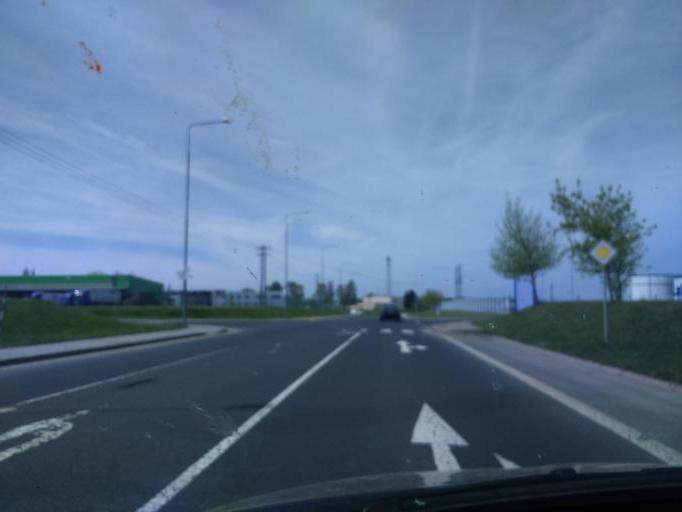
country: CZ
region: Karlovarsky
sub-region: Okres Cheb
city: Cheb
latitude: 50.0867
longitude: 12.4099
